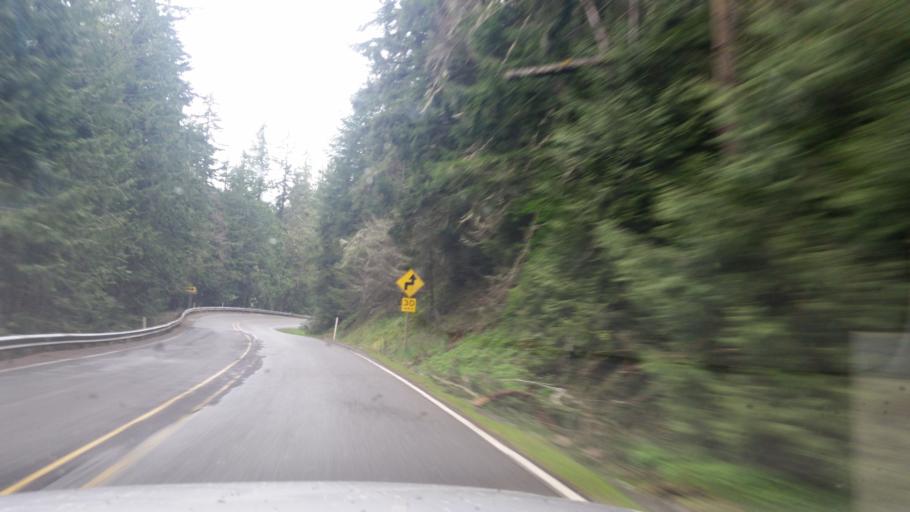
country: US
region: Washington
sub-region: Pierce County
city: Eatonville
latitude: 46.8252
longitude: -122.3006
